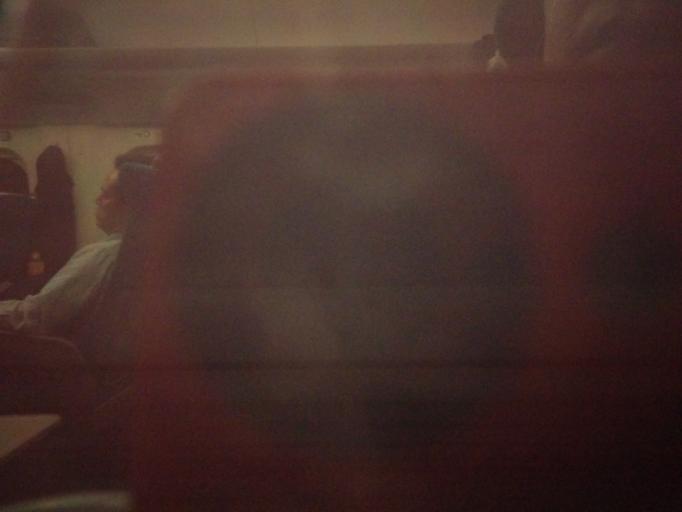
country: JP
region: Shizuoka
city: Mishima
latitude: 35.1208
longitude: 138.9432
